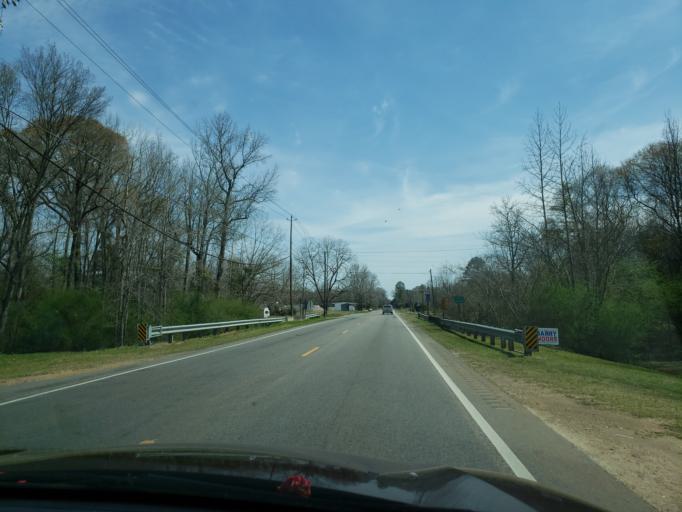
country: US
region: Alabama
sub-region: Autauga County
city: Prattville
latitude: 32.4308
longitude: -86.5042
